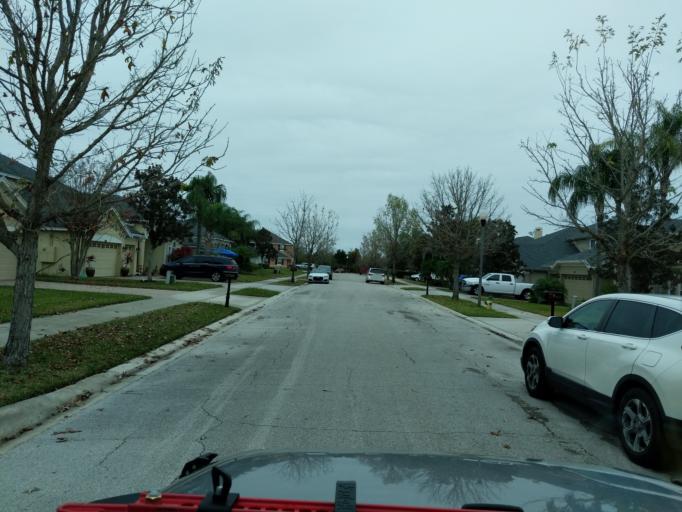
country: US
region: Florida
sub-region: Orange County
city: Winter Garden
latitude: 28.5281
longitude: -81.5775
